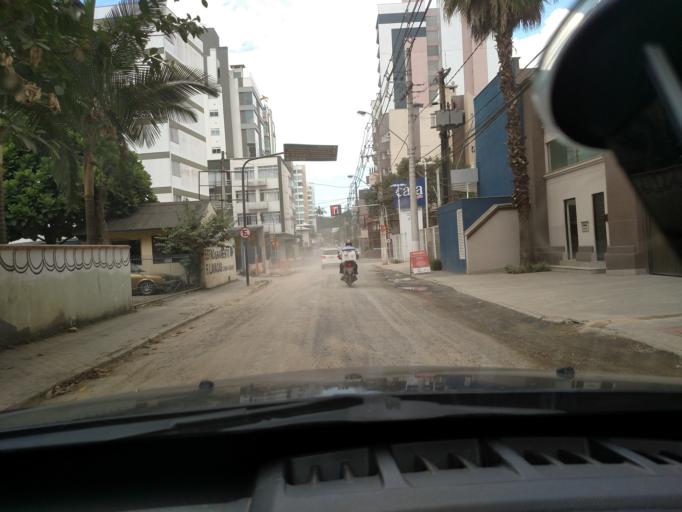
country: BR
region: Santa Catarina
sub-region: Blumenau
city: Blumenau
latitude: -26.9257
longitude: -49.0635
